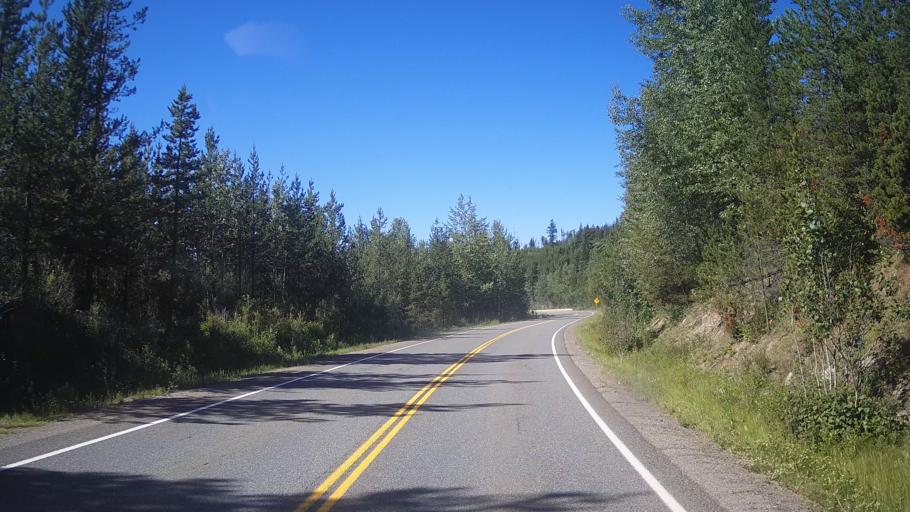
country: CA
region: British Columbia
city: Kamloops
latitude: 51.4861
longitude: -120.4637
